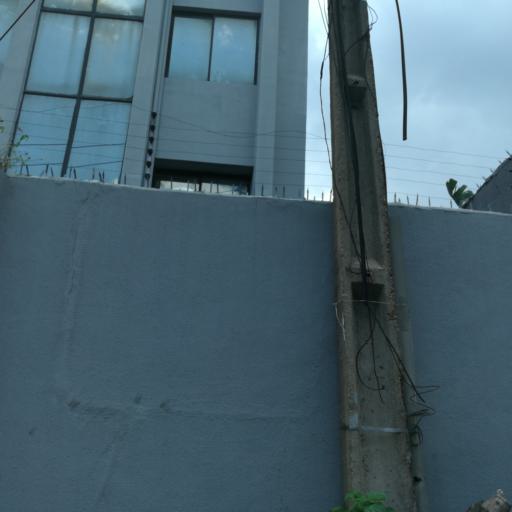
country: NG
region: Lagos
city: Somolu
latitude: 6.5569
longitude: 3.3677
